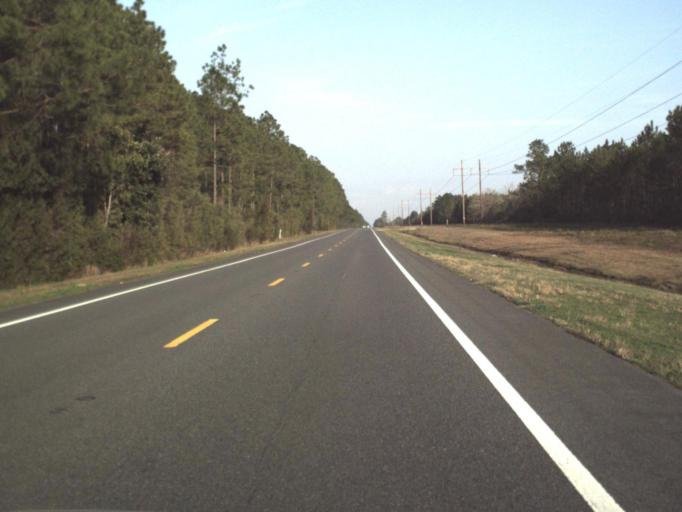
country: US
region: Florida
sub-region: Bay County
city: Laguna Beach
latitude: 30.4398
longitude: -85.7964
